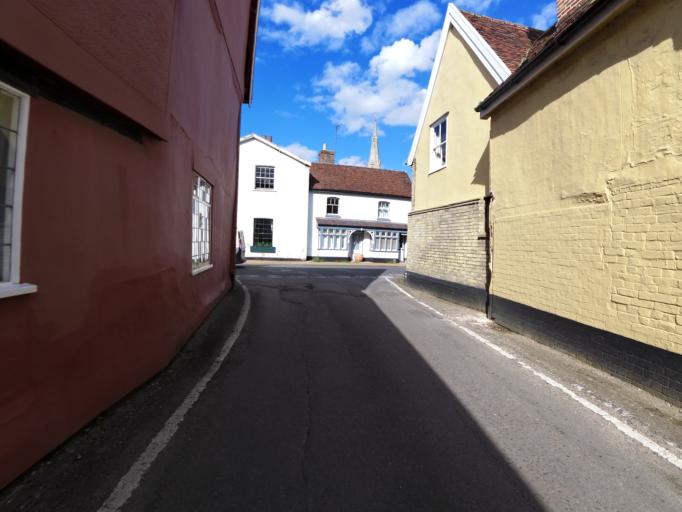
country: GB
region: England
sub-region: Suffolk
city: Woolpit
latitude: 52.2245
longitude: 0.8877
